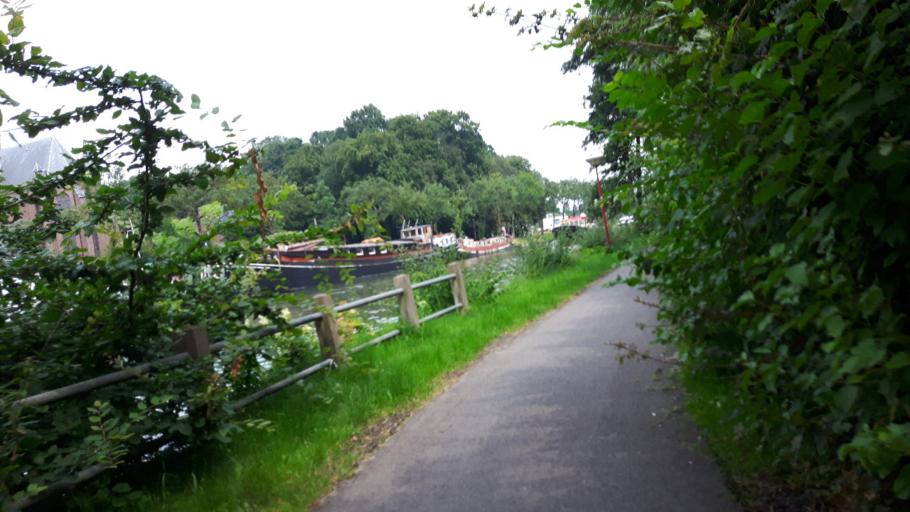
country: NL
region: Utrecht
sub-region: Gemeente Nieuwegein
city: Nieuwegein
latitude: 52.0388
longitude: 5.0968
